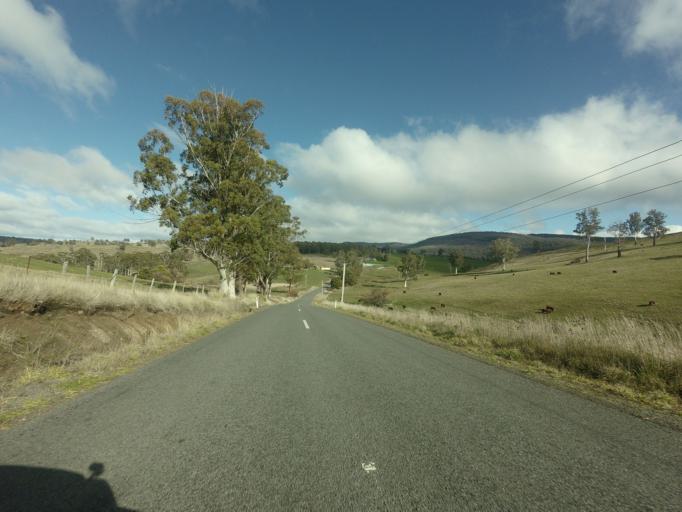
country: AU
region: Tasmania
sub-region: Derwent Valley
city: New Norfolk
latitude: -42.5638
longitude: 146.7045
